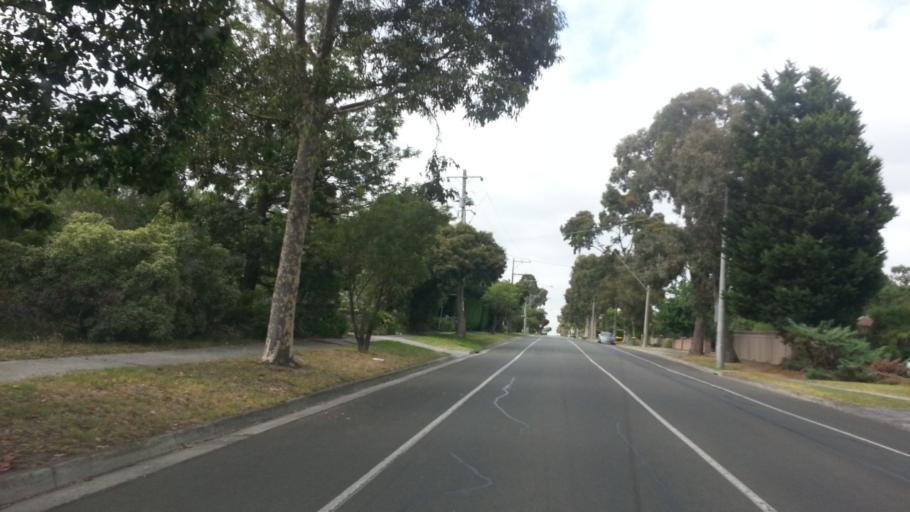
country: AU
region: Victoria
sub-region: Knox
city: Rowville
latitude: -37.9205
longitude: 145.2454
